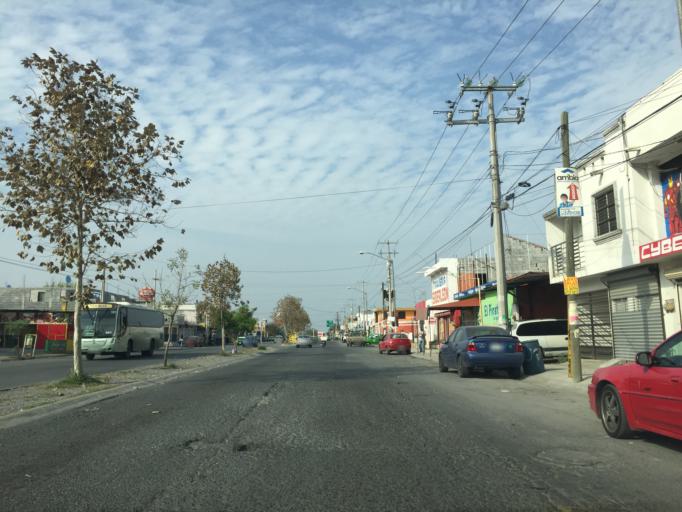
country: MX
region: Nuevo Leon
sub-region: Apodaca
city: Fraccionamiento Cosmopolis Octavo Sector
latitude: 25.7942
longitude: -100.2486
